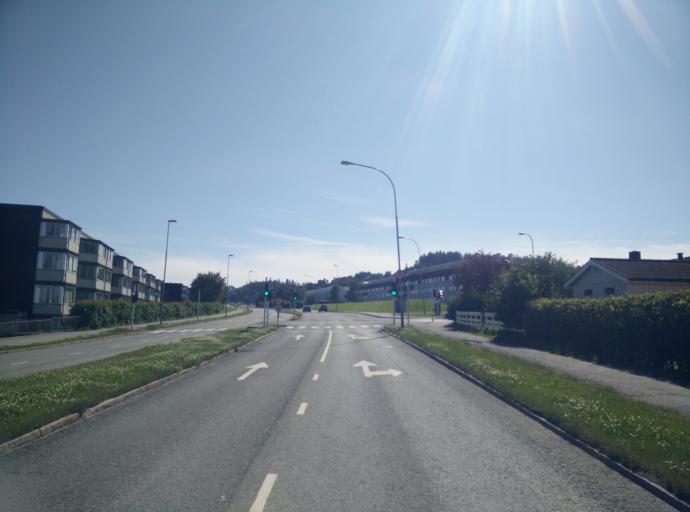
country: NO
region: Sor-Trondelag
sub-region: Trondheim
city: Trondheim
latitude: 63.4121
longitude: 10.3619
